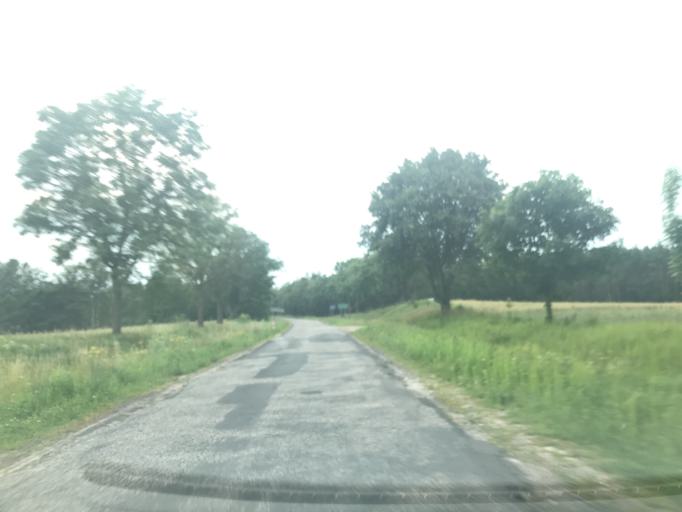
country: PL
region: Kujawsko-Pomorskie
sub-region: Powiat lipnowski
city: Lipno
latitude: 52.7977
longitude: 19.2036
